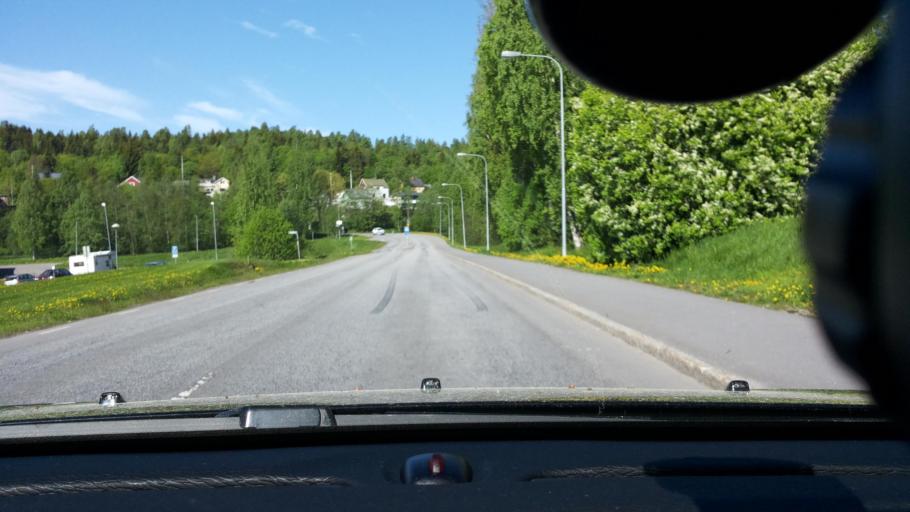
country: SE
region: Vaesternorrland
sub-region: Sundsvalls Kommun
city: Sundsbruk
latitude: 62.4584
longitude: 17.3531
